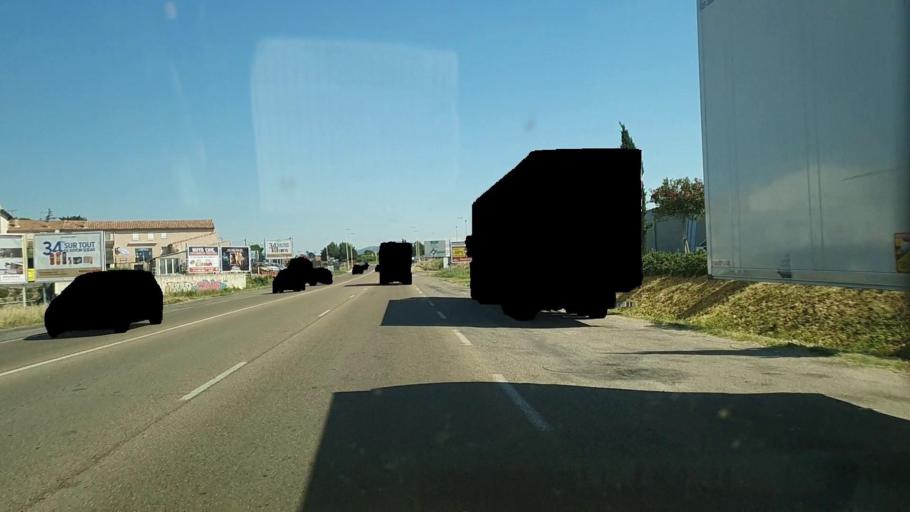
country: FR
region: Languedoc-Roussillon
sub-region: Departement du Gard
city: Ales
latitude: 44.1270
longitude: 4.1069
